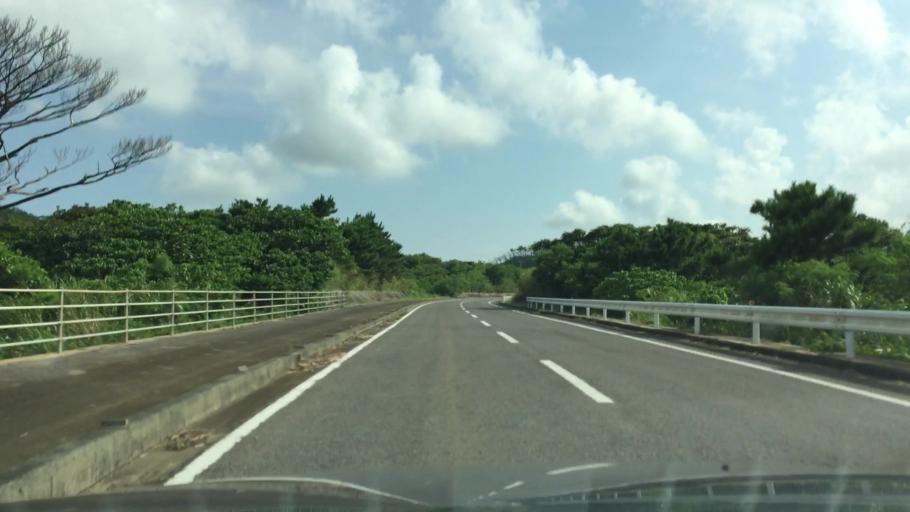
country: JP
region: Okinawa
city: Ishigaki
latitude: 24.4132
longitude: 124.2304
